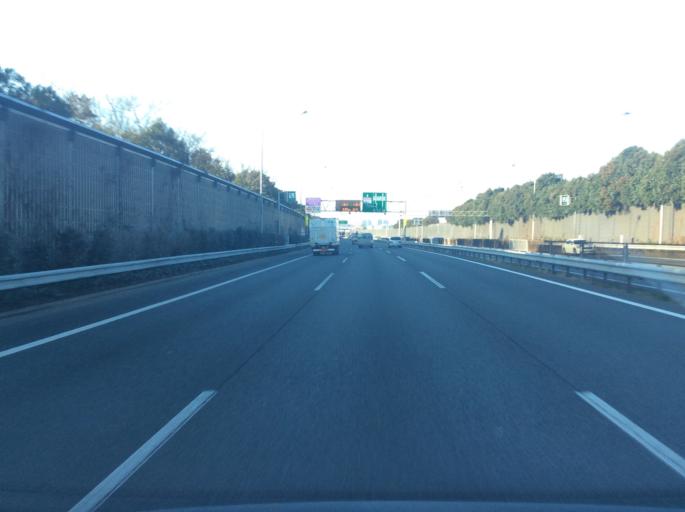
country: JP
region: Chiba
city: Nagareyama
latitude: 35.8709
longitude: 139.8874
